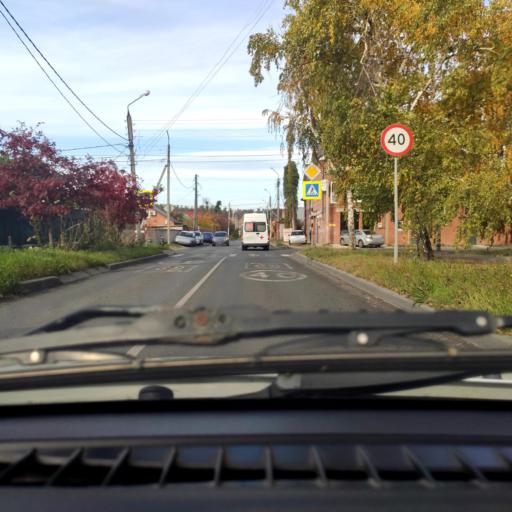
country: RU
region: Samara
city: Tol'yatti
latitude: 53.5077
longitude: 49.3985
